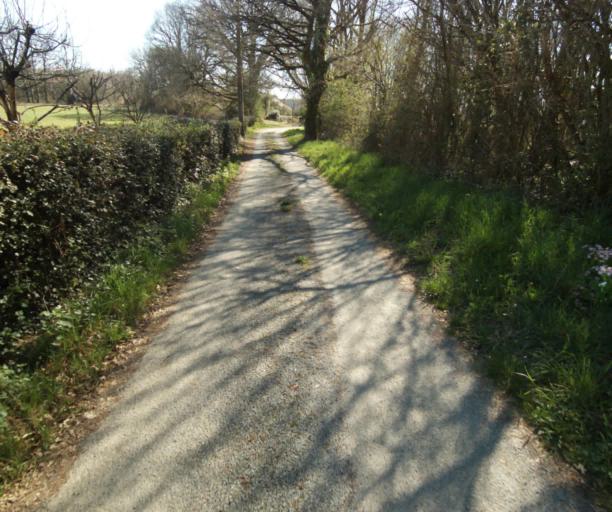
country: FR
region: Limousin
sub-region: Departement de la Correze
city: Chamboulive
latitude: 45.4648
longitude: 1.7473
